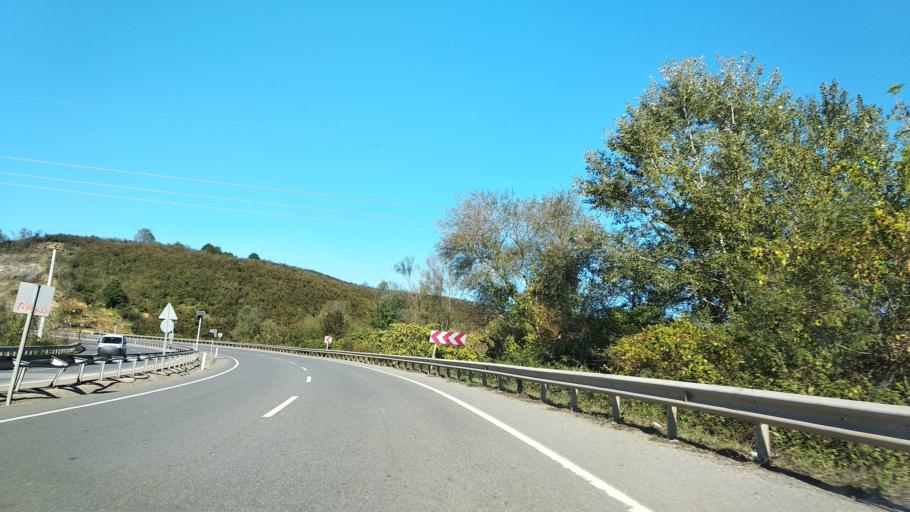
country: TR
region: Sakarya
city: Karasu
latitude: 41.0824
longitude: 30.6476
